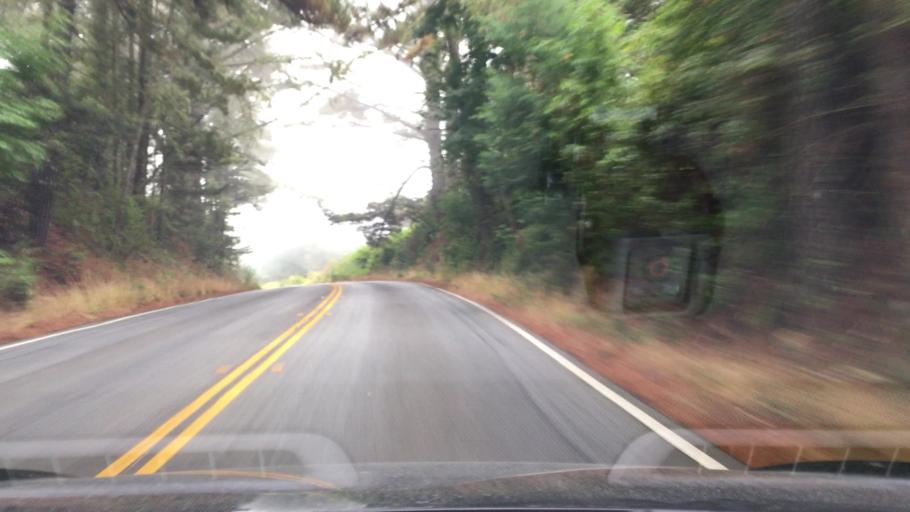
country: US
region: California
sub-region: San Mateo County
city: Highlands-Baywood Park
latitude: 37.4706
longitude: -122.3554
